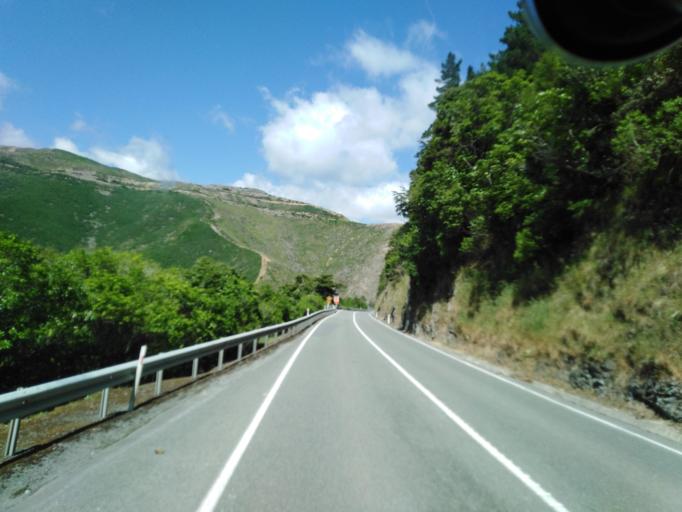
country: NZ
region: Nelson
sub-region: Nelson City
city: Nelson
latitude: -41.2287
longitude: 173.4159
